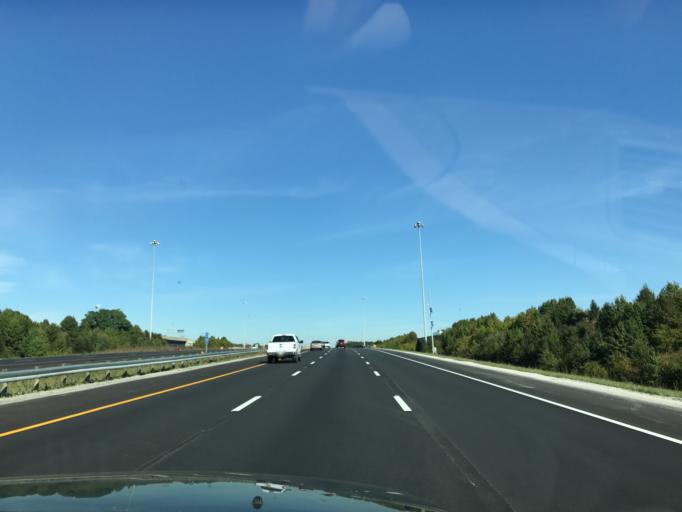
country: US
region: Ohio
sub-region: Franklin County
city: Huber Ridge
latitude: 40.0551
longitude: -82.9027
